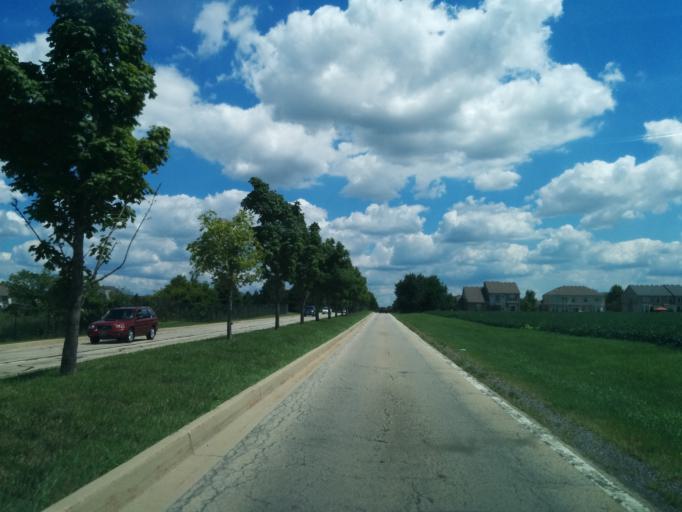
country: US
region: Illinois
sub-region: Will County
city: Plainfield
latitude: 41.6816
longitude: -88.1584
